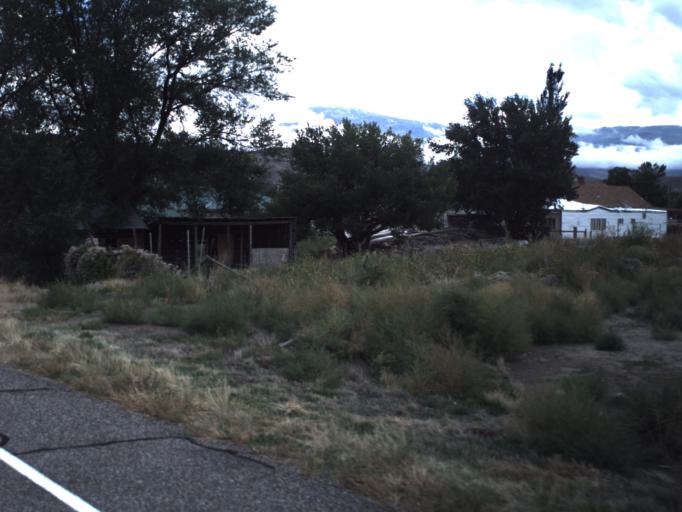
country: US
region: Utah
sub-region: Sevier County
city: Monroe
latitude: 38.6242
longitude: -112.2196
